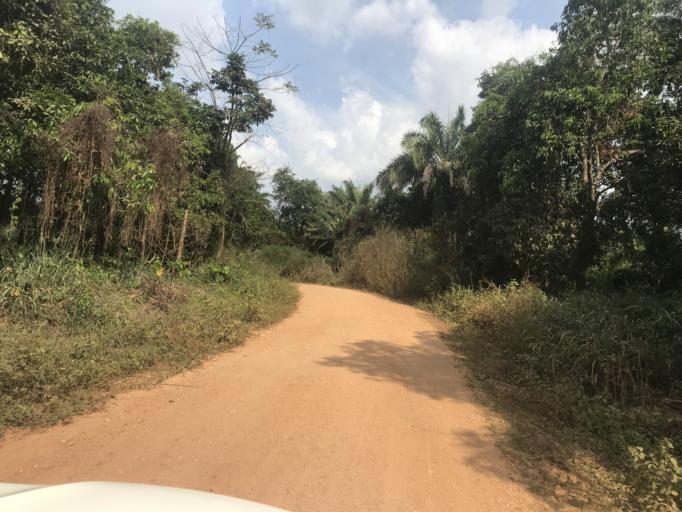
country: NG
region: Osun
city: Inisa
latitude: 7.8813
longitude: 4.3893
